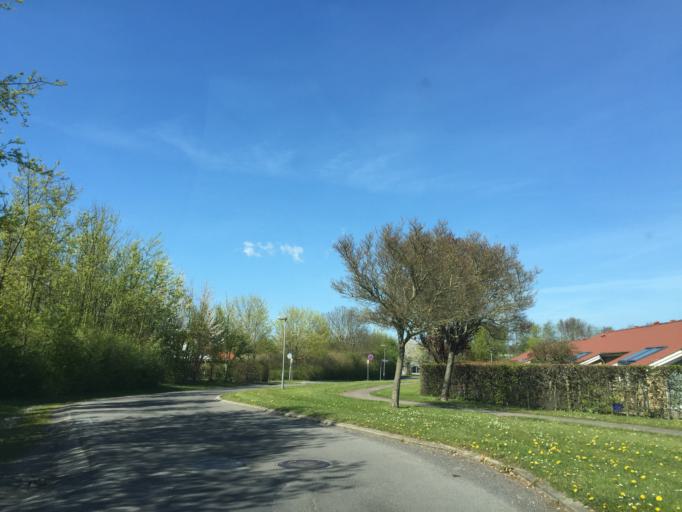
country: DK
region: South Denmark
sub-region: Odense Kommune
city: Odense
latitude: 55.3672
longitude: 10.3985
